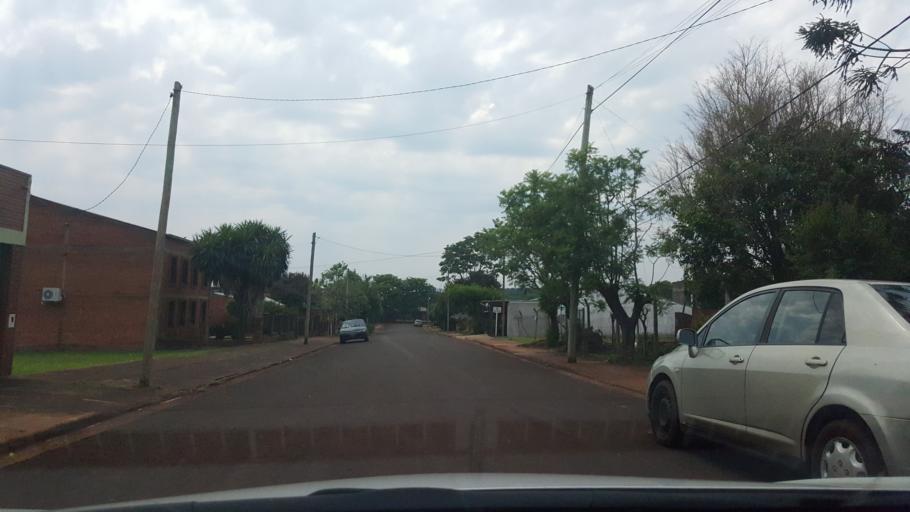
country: AR
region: Misiones
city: Capiovi
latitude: -26.9334
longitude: -55.0573
